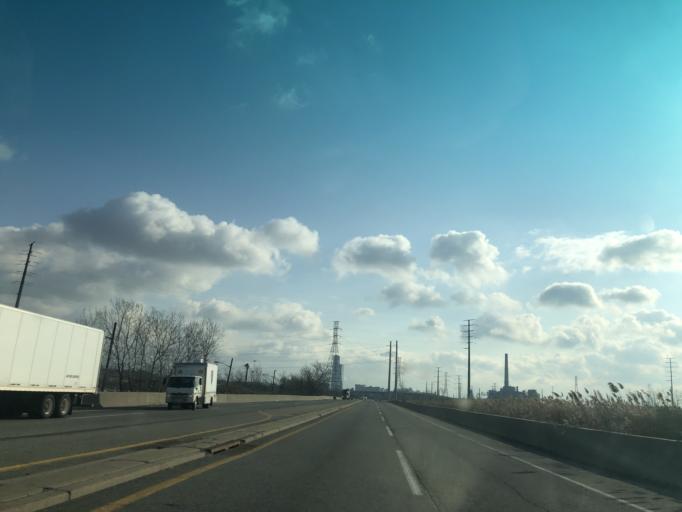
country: US
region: New Jersey
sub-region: Hudson County
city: Secaucus
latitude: 40.7619
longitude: -74.0727
